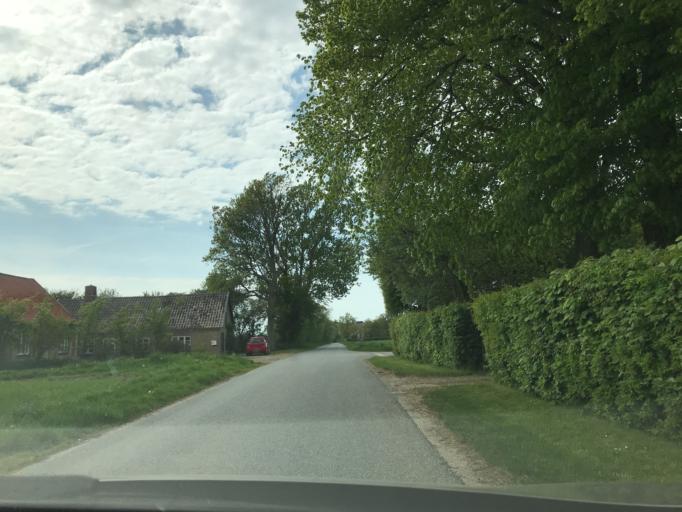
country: DK
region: South Denmark
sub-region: Middelfart Kommune
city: Norre Aby
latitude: 55.3637
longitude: 9.8441
